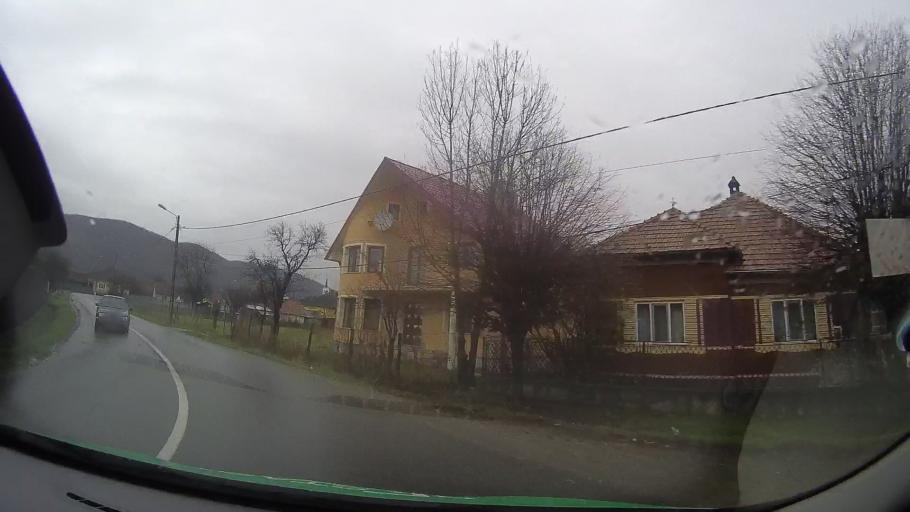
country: RO
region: Bistrita-Nasaud
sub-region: Municipiul Bistrita
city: Viisoara
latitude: 47.0688
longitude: 24.4379
